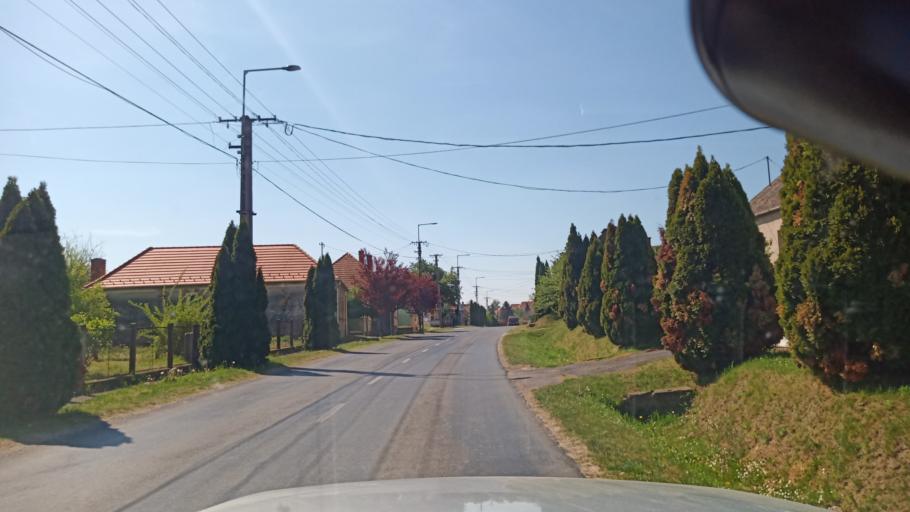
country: HU
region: Zala
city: Sarmellek
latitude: 46.7449
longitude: 17.1070
